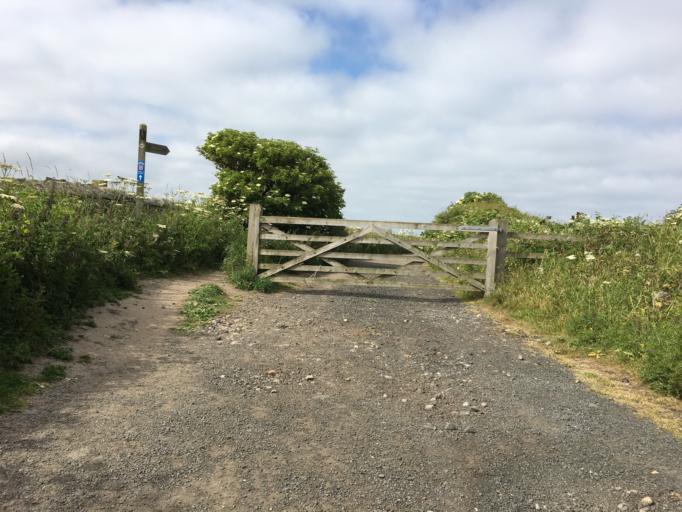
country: GB
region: England
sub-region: Northumberland
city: Alnmouth
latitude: 55.4242
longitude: -1.5808
